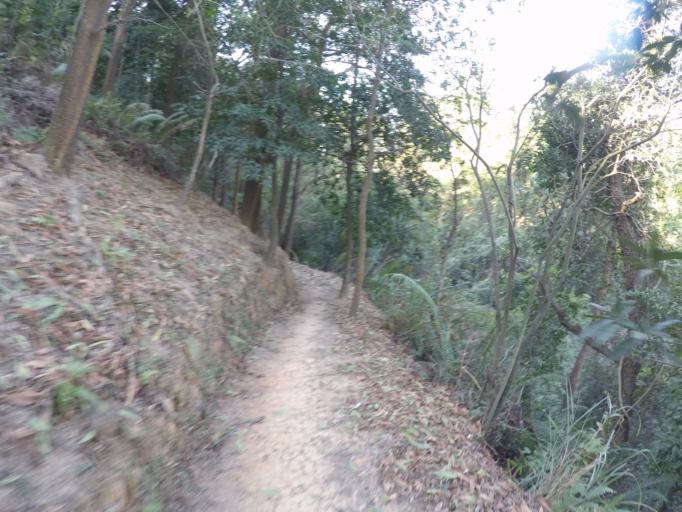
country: CN
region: Guangdong
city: Huancheng
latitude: 22.4756
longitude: 113.4148
